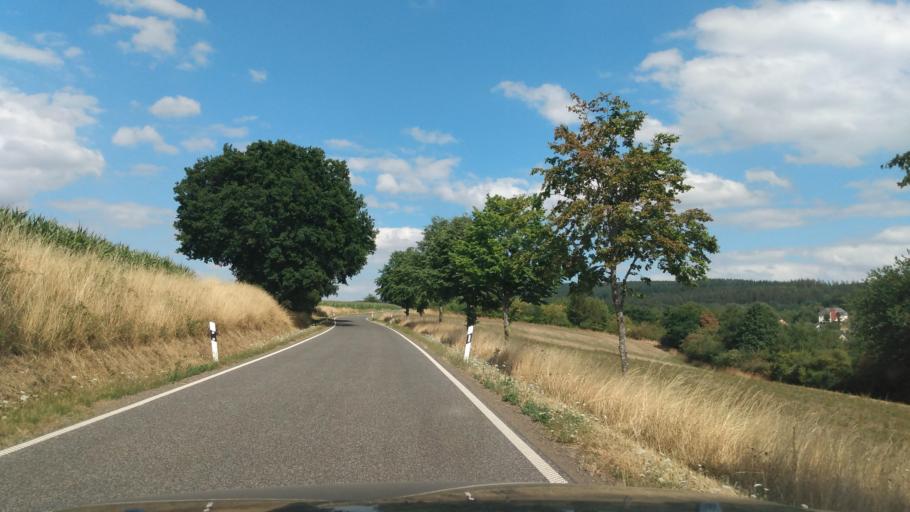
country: DE
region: Rheinland-Pfalz
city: Rorodt
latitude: 49.7771
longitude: 7.0899
